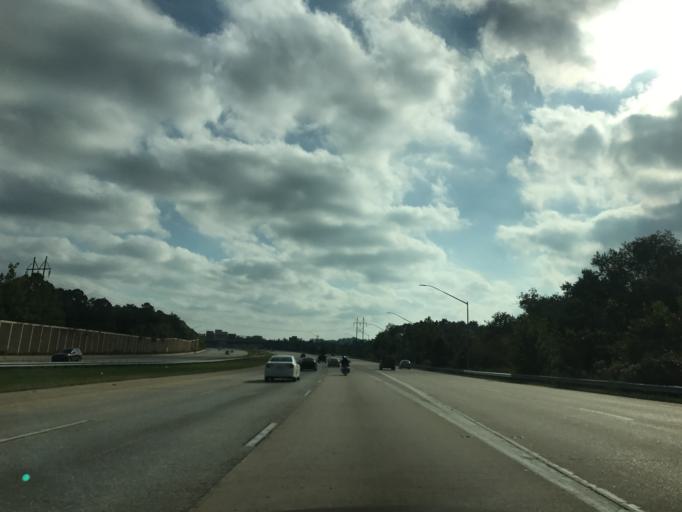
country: US
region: Maryland
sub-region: Anne Arundel County
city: Glen Burnie
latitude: 39.1607
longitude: -76.6449
